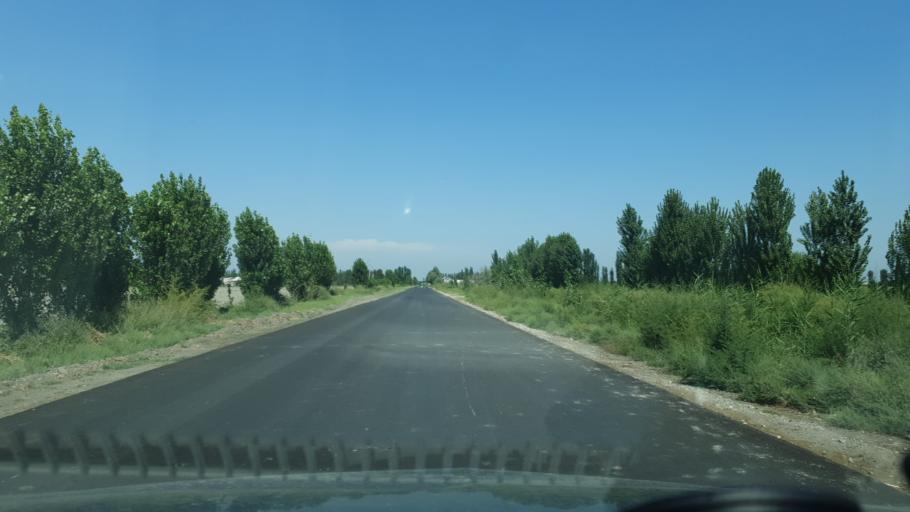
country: UZ
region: Namangan
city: Pop
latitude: 40.6174
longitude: 71.2007
